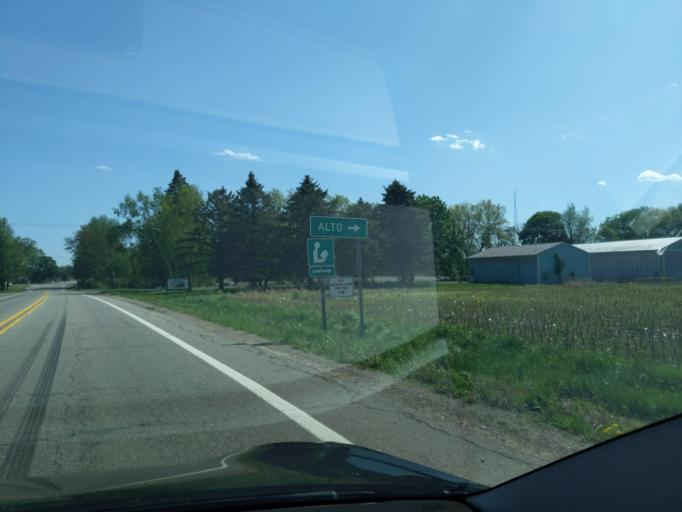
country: US
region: Michigan
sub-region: Kent County
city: Lowell
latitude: 42.8576
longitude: -85.3709
